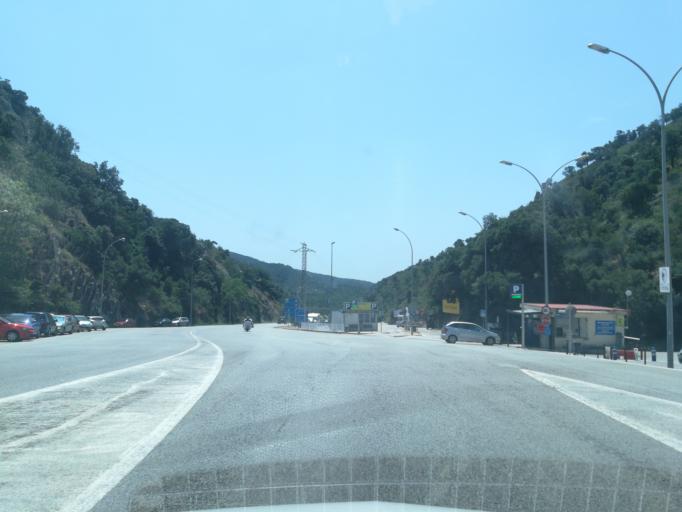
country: ES
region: Catalonia
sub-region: Provincia de Girona
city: la Jonquera
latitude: 42.4589
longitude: 2.8641
